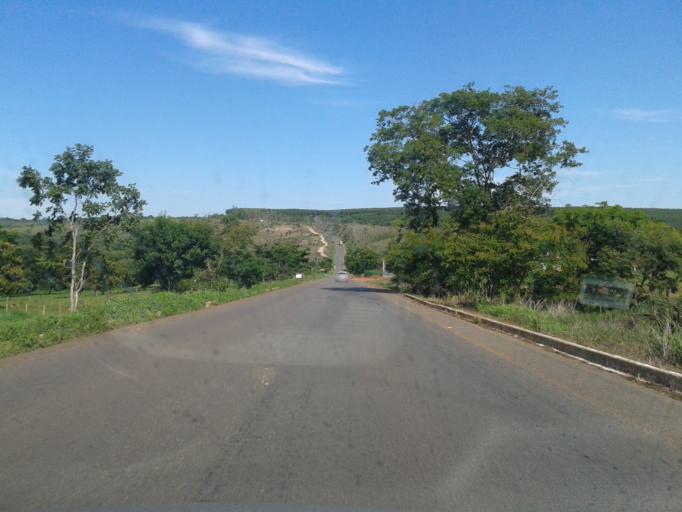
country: BR
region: Goias
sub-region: Bela Vista De Goias
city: Bela Vista de Goias
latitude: -17.1752
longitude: -48.7224
